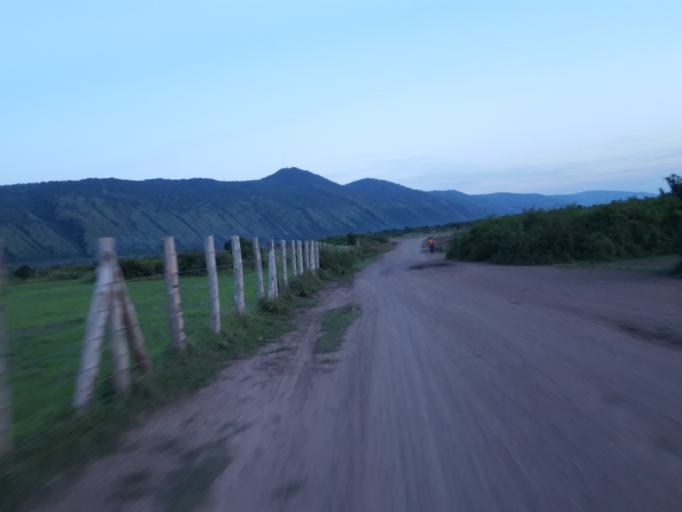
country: UG
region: Western Region
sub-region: Kibale District
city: Kagadi
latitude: 1.2415
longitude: 30.7467
